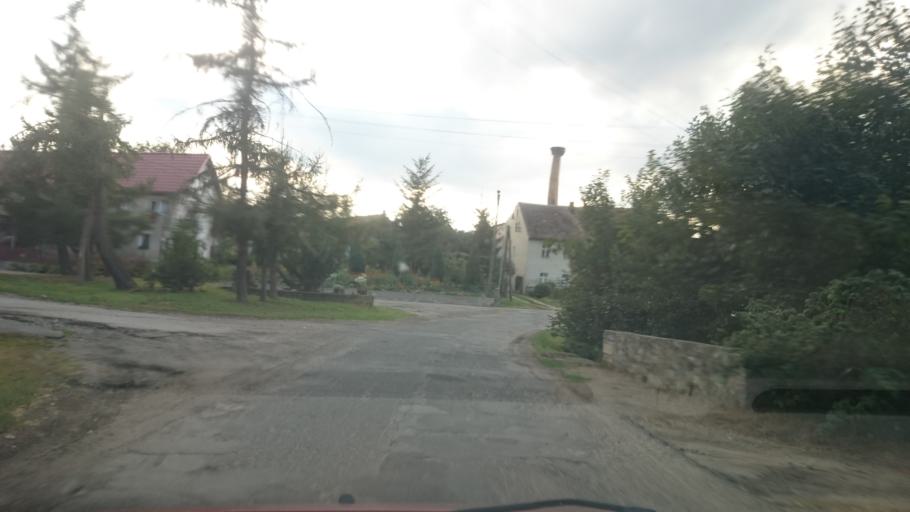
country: PL
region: Lower Silesian Voivodeship
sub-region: Powiat zabkowicki
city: Ziebice
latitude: 50.5501
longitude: 17.0531
